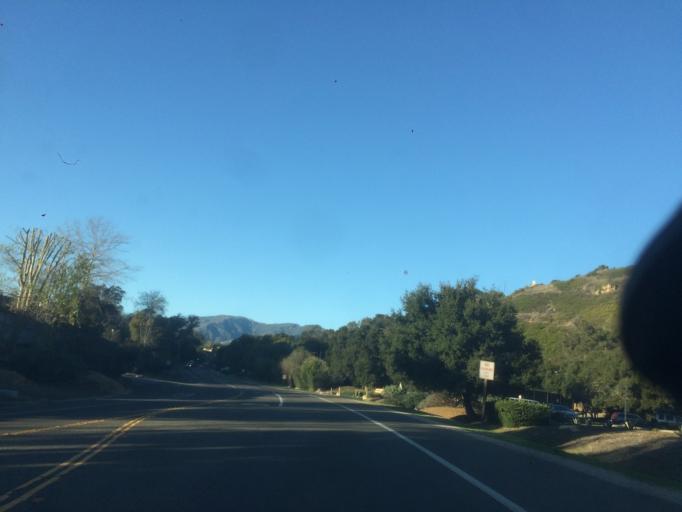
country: US
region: California
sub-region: Santa Barbara County
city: Santa Barbara
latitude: 34.4141
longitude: -119.7401
